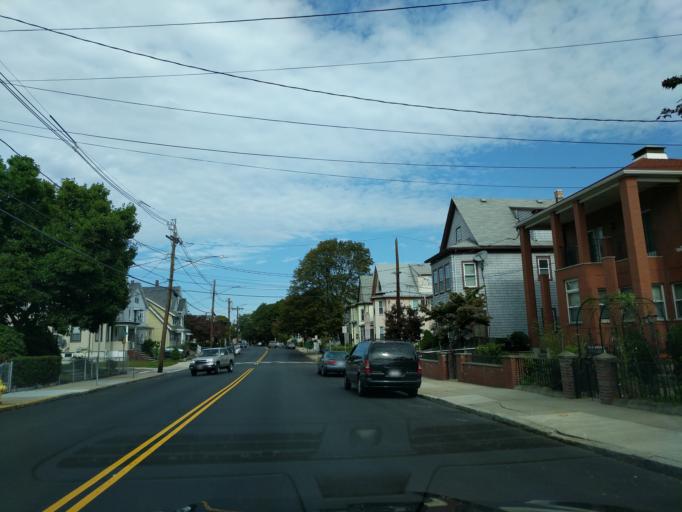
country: US
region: Massachusetts
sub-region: Suffolk County
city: Chelsea
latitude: 42.4071
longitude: -71.0294
